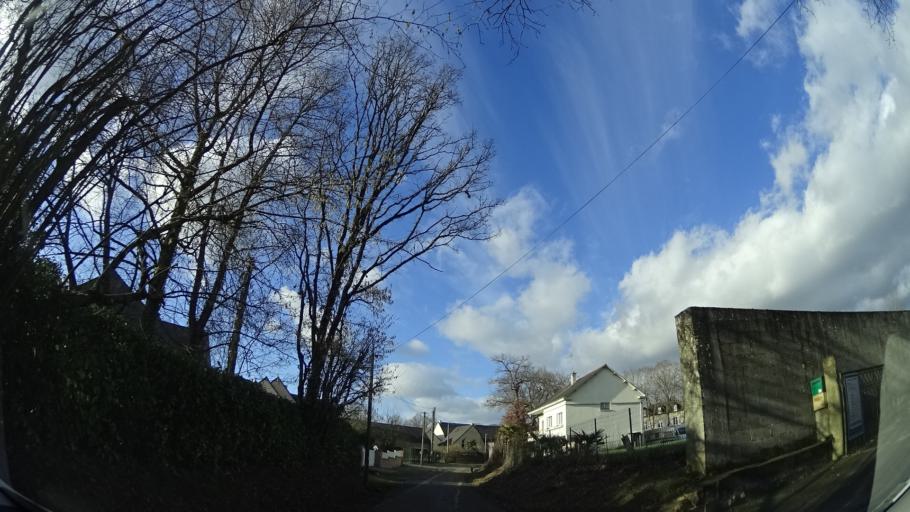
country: FR
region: Brittany
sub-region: Departement d'Ille-et-Vilaine
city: Cesson-Sevigne
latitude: 48.1342
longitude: -1.6358
